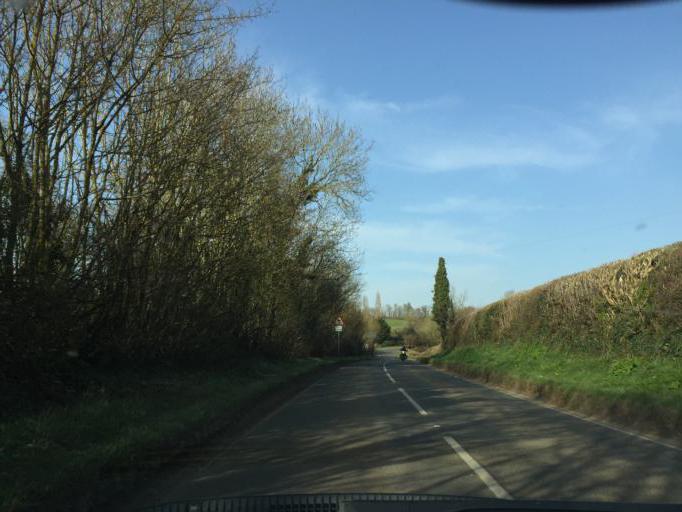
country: GB
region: England
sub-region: Oxfordshire
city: Bloxham
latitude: 52.0477
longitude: -1.3793
